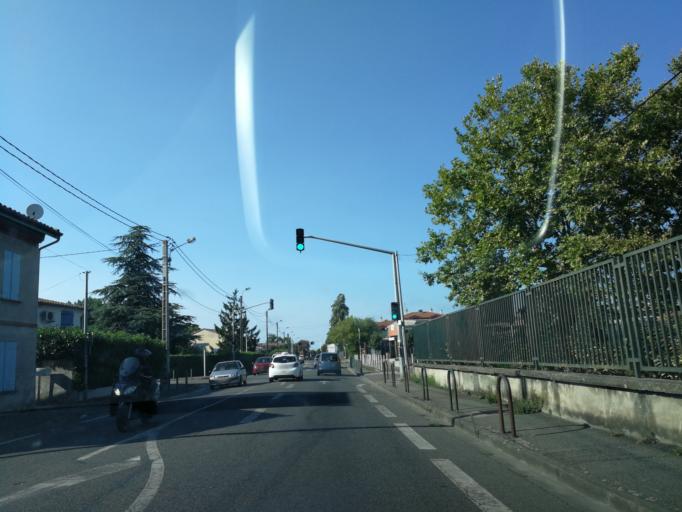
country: FR
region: Midi-Pyrenees
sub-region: Departement de la Haute-Garonne
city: Aucamville
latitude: 43.6390
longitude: 1.4393
